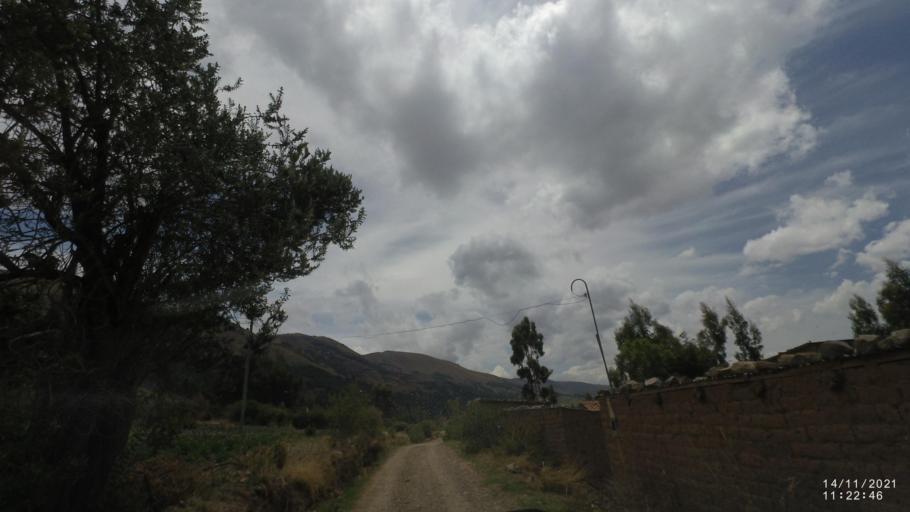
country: BO
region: Cochabamba
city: Cochabamba
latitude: -17.3354
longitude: -66.0320
